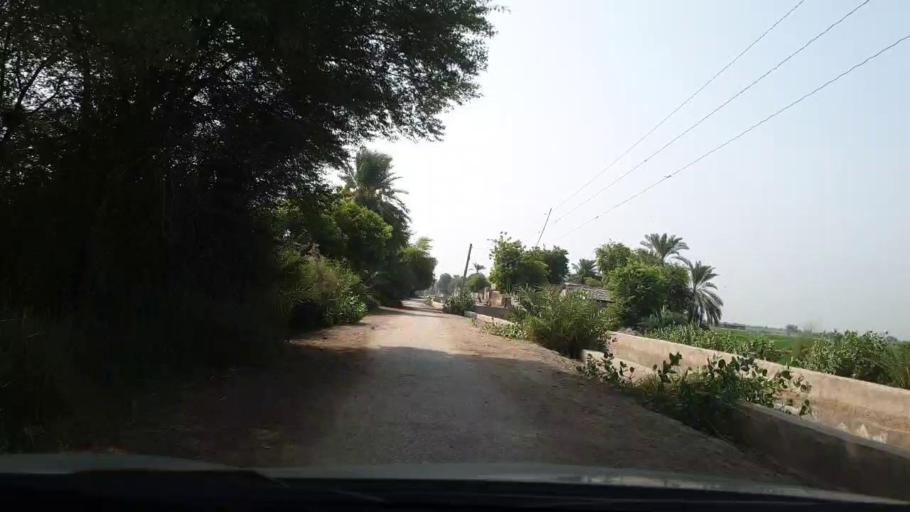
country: PK
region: Sindh
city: Larkana
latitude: 27.4679
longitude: 68.2417
